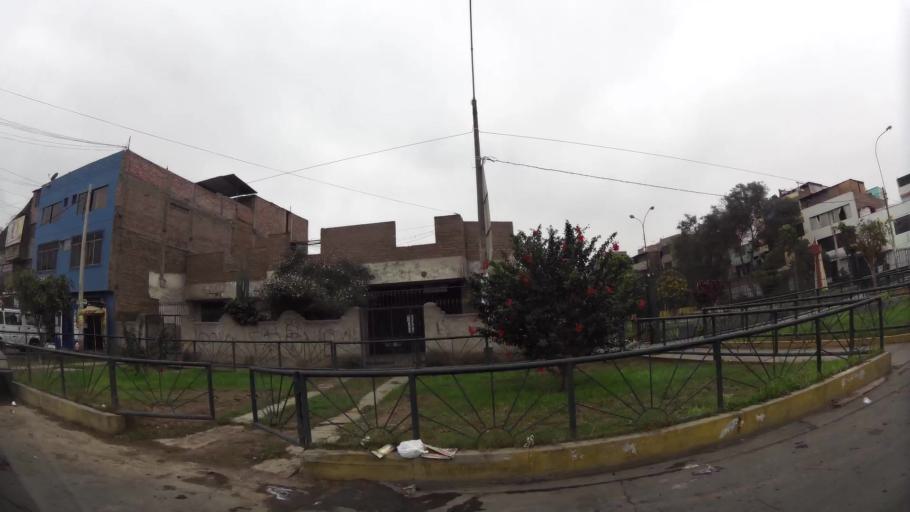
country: PE
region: Lima
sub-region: Lima
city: San Luis
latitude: -12.0710
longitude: -77.0089
